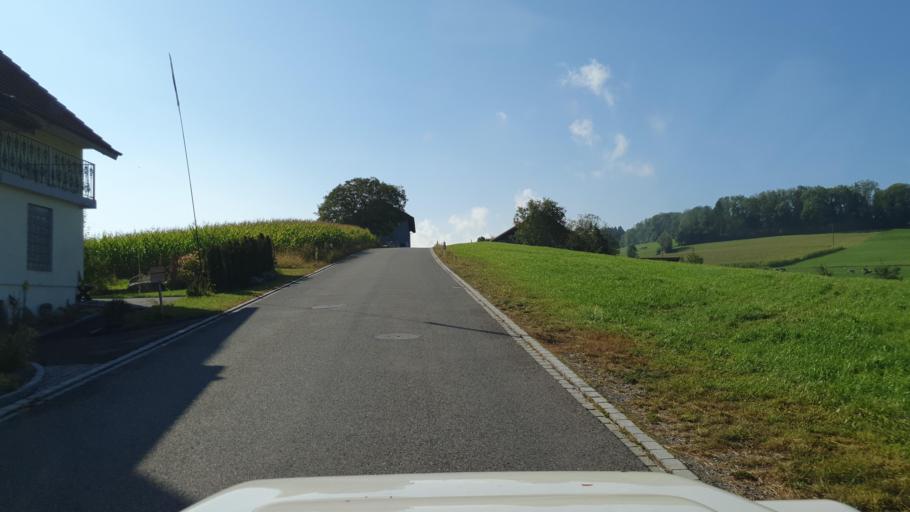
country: CH
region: Aargau
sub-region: Bezirk Muri
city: Waltenschwil
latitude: 47.3166
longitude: 8.2917
